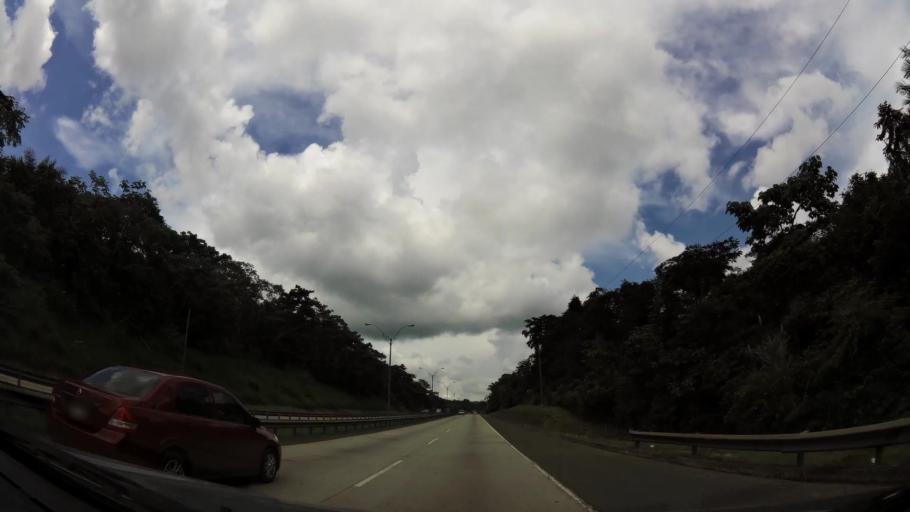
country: PA
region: Panama
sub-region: Distrito Arraijan
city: Arraijan
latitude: 8.9764
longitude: -79.6450
